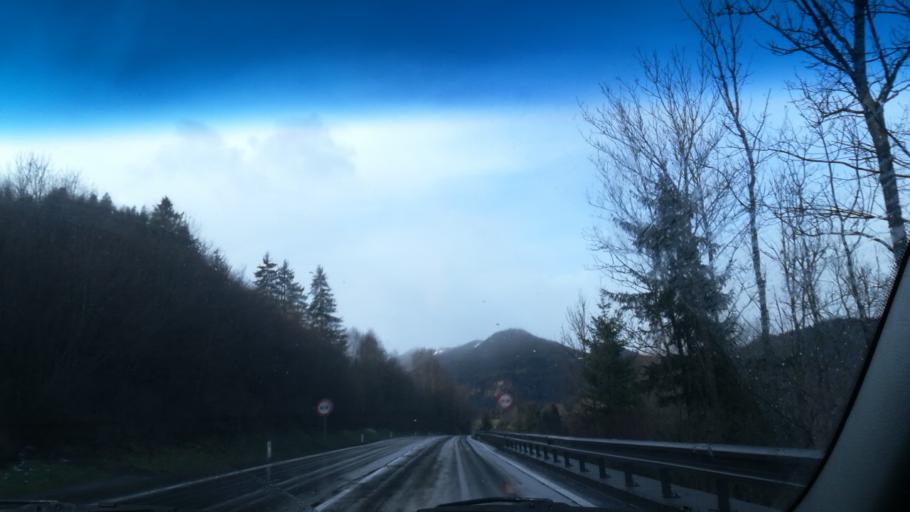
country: AT
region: Styria
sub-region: Politischer Bezirk Murtal
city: Sankt Peter ob Judenburg
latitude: 47.1963
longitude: 14.5738
